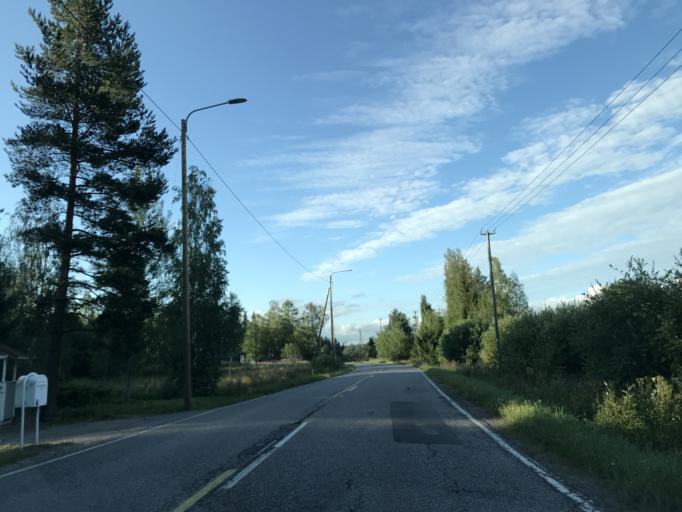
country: FI
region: Uusimaa
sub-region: Helsinki
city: Nurmijaervi
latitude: 60.3690
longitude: 24.6816
